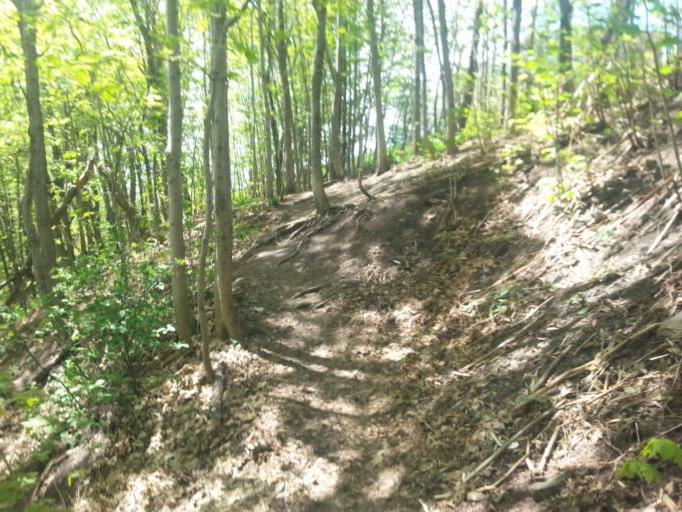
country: CA
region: Quebec
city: Quebec
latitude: 46.7718
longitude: -71.2547
